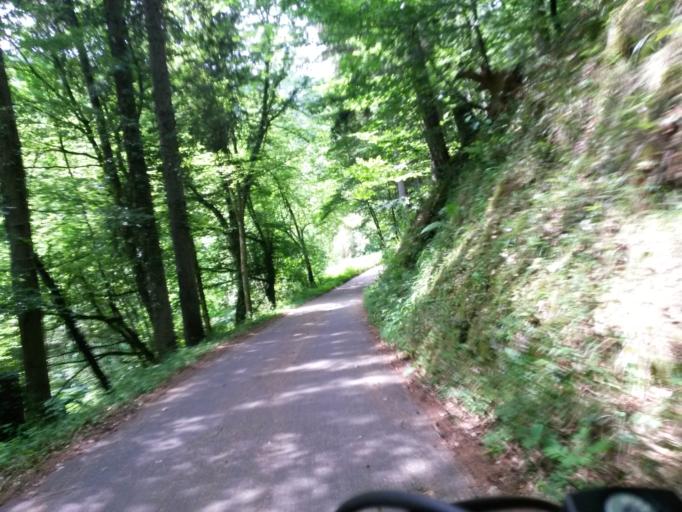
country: DE
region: Baden-Wuerttemberg
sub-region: Karlsruhe Region
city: Calw
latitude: 48.6723
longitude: 8.7393
